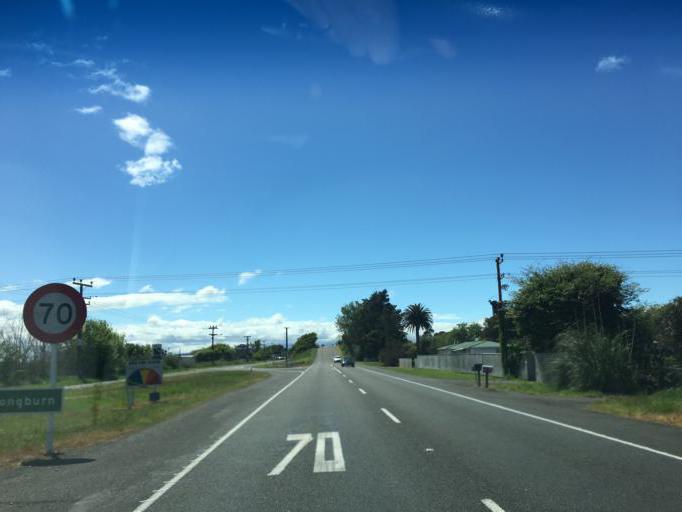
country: NZ
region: Manawatu-Wanganui
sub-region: Palmerston North City
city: Palmerston North
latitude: -40.3866
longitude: 175.5365
